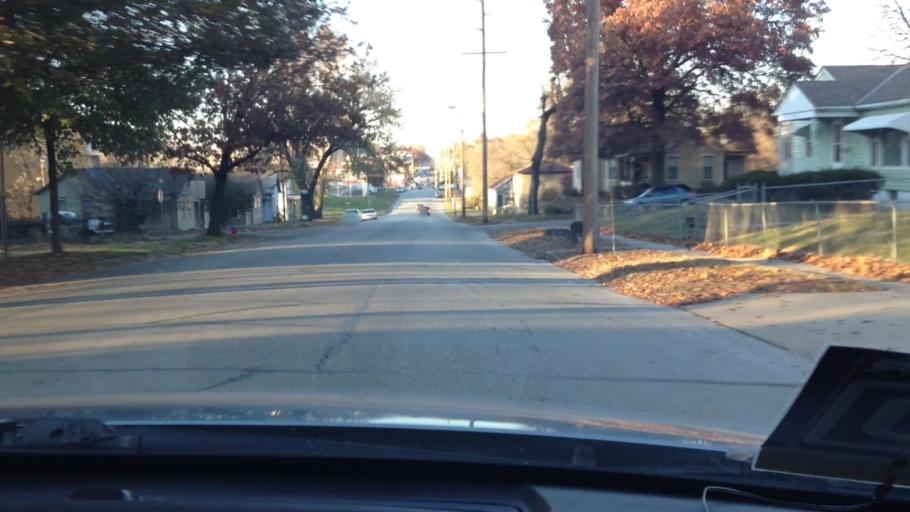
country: US
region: Kansas
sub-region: Leavenworth County
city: Leavenworth
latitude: 39.3118
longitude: -94.9092
